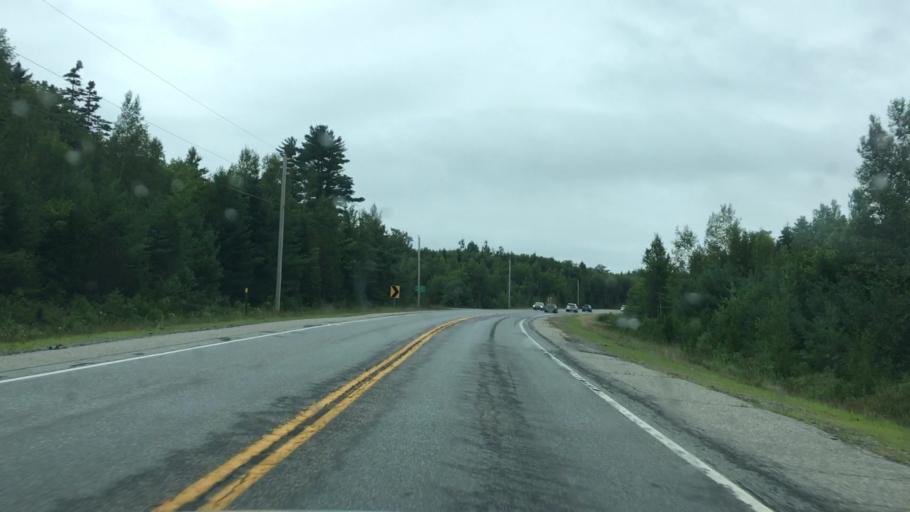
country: US
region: Maine
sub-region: Washington County
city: Cherryfield
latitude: 44.8520
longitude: -68.0596
